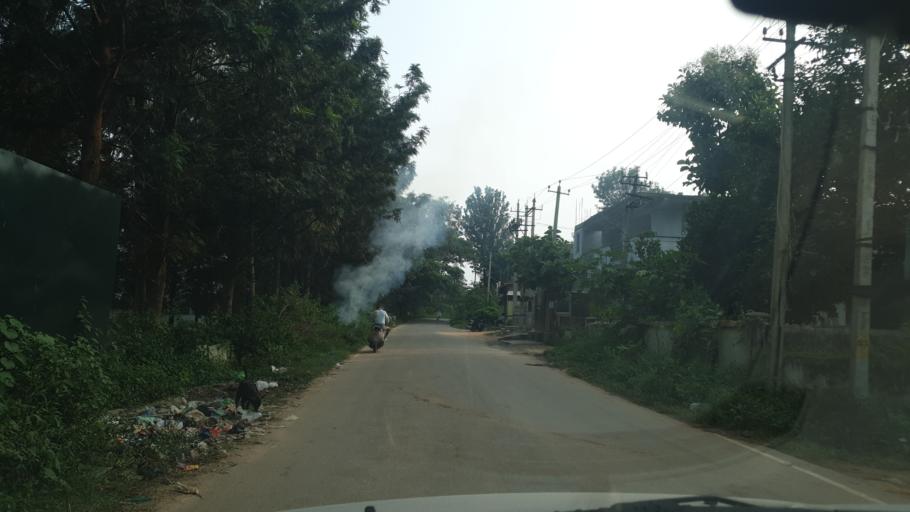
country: IN
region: Karnataka
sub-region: Bangalore Urban
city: Yelahanka
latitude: 13.0706
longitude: 77.6711
